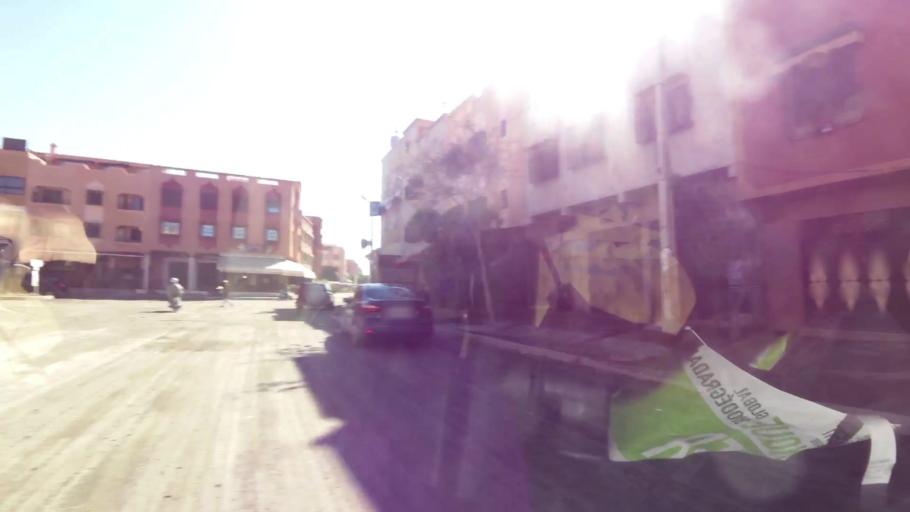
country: MA
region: Marrakech-Tensift-Al Haouz
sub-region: Marrakech
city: Marrakesh
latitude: 31.5967
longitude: -8.0452
